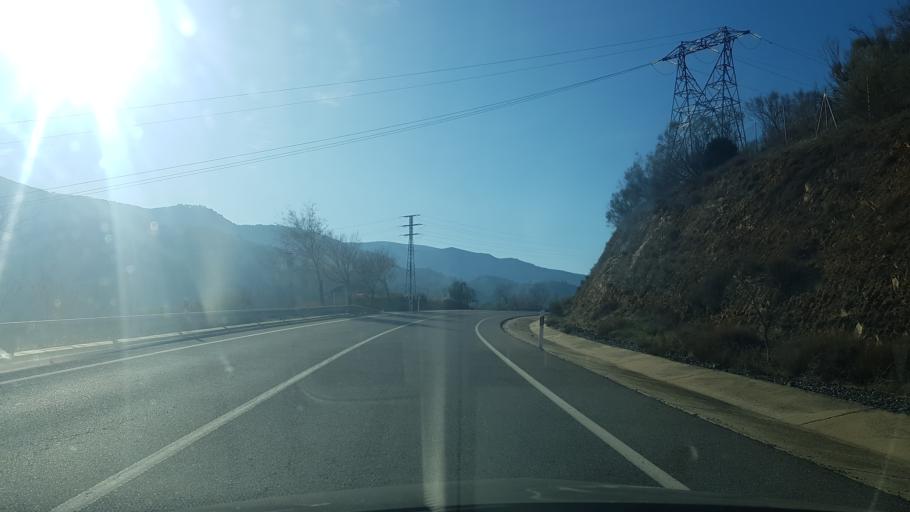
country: ES
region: Castille and Leon
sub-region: Provincia de Avila
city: El Tiemblo
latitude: 40.4284
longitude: -4.5285
